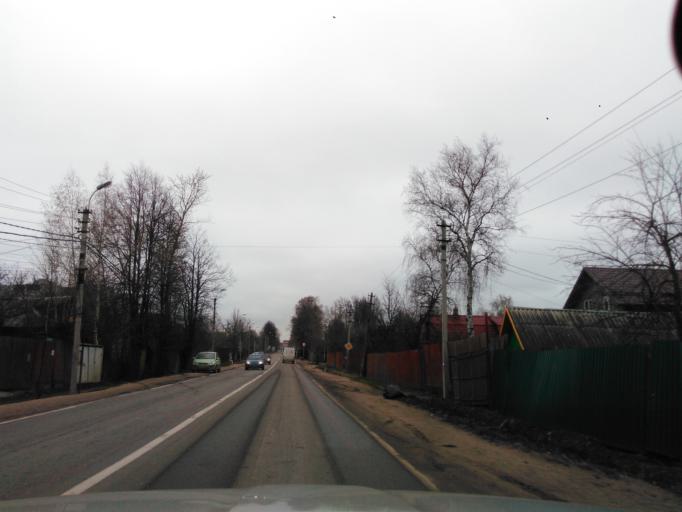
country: RU
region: Moskovskaya
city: Nakhabino
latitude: 55.8437
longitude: 37.1869
